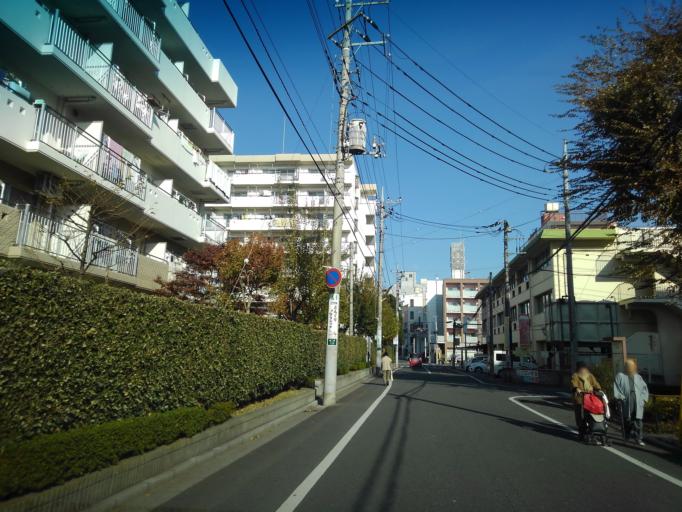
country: JP
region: Saitama
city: Tokorozawa
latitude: 35.8039
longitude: 139.4543
